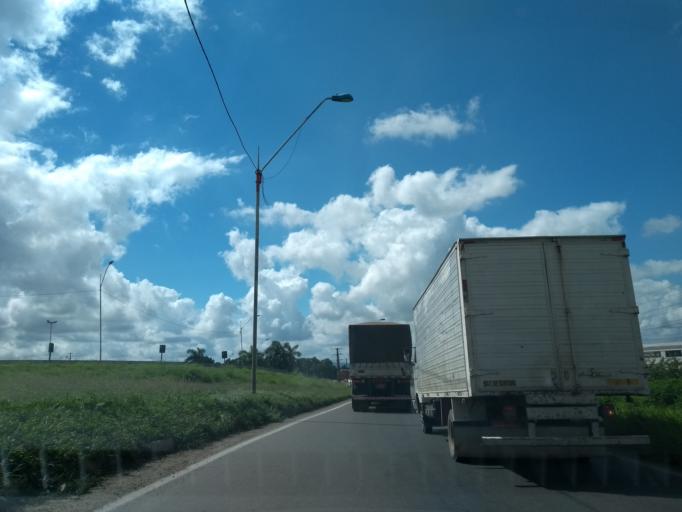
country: BR
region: Bahia
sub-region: Feira De Santana
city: Feira de Santana
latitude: -12.2733
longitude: -38.9363
